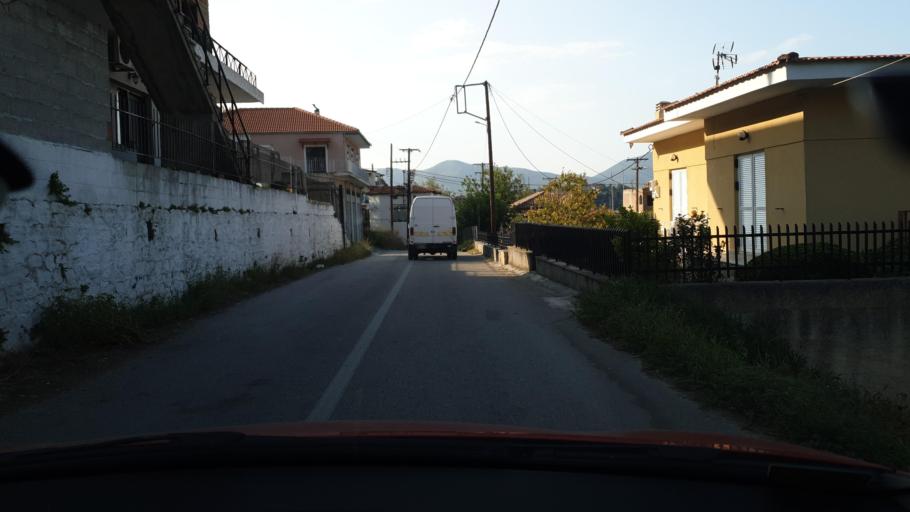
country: GR
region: Thessaly
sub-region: Nomos Magnisias
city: Pteleos
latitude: 39.0036
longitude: 22.9636
